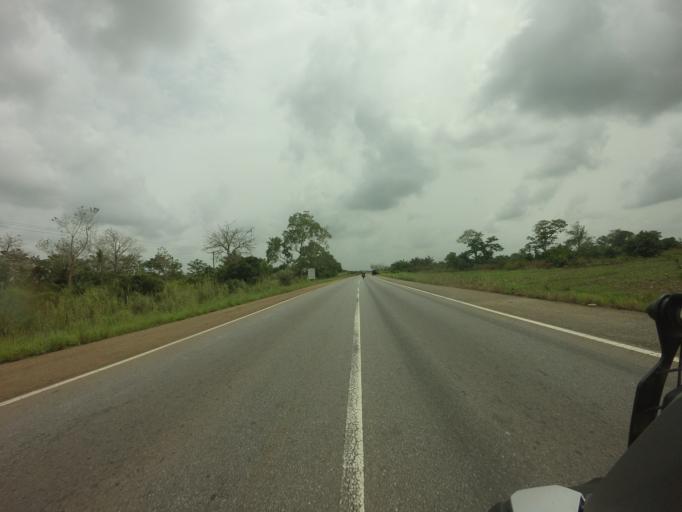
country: GH
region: Volta
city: Keta
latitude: 6.0897
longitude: 0.7459
